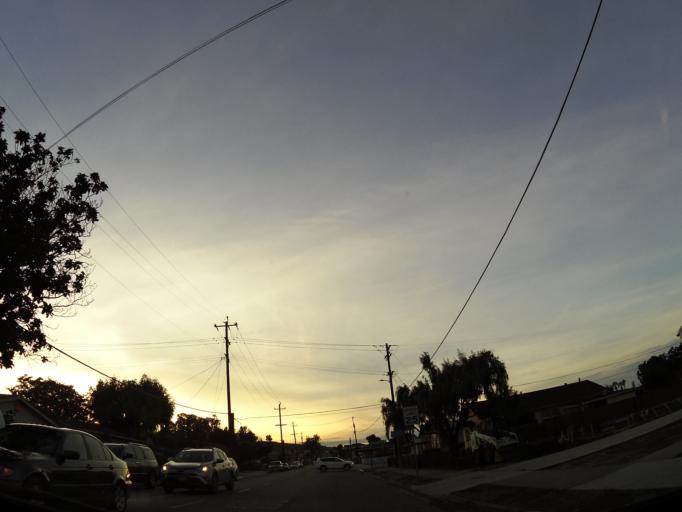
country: US
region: California
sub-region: San Benito County
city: Hollister
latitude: 36.8566
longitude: -121.3992
